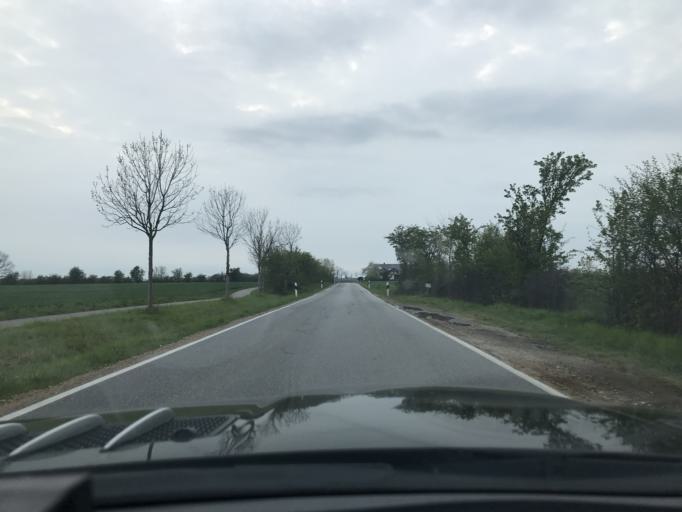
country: DE
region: Schleswig-Holstein
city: Burg auf Fehmarn
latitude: 54.4296
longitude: 11.2254
